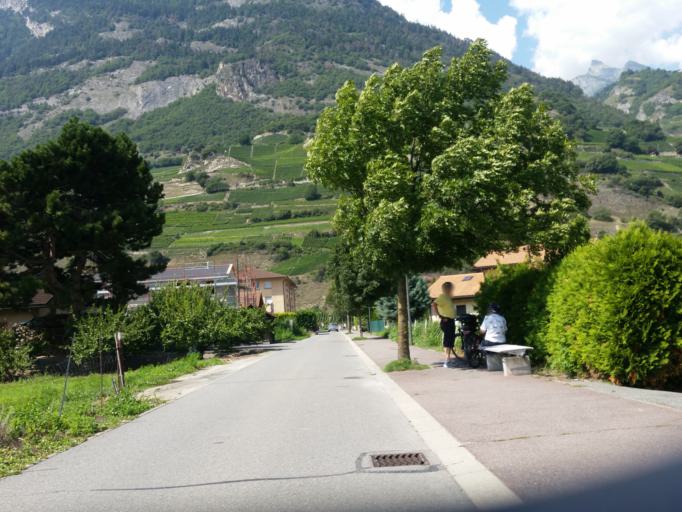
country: CH
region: Valais
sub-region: Martigny District
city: Saillon
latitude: 46.1724
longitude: 7.1920
